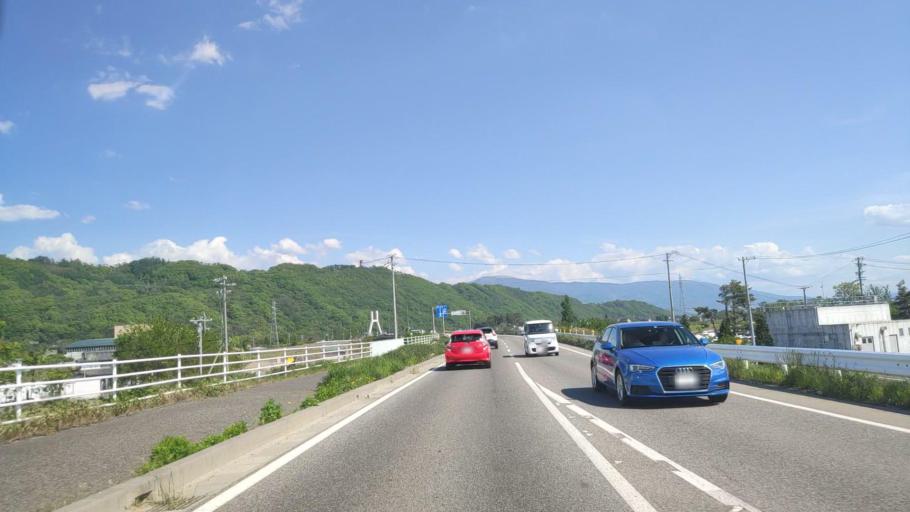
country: JP
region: Nagano
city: Toyoshina
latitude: 36.2713
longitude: 137.9346
